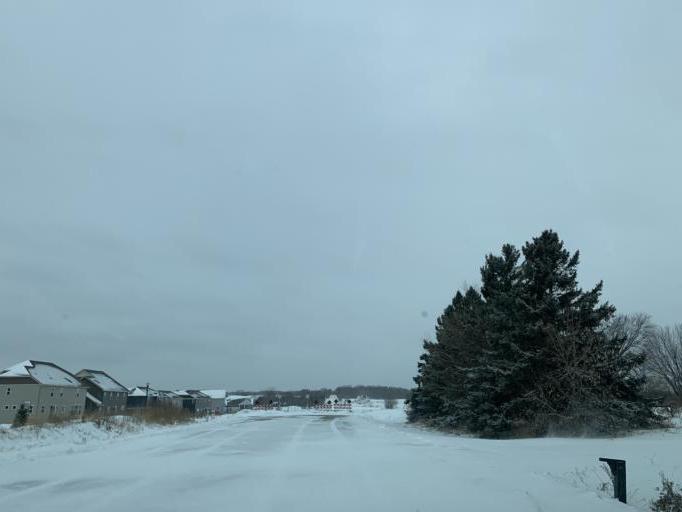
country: US
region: Minnesota
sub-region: Washington County
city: Cottage Grove
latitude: 44.8522
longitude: -92.9080
